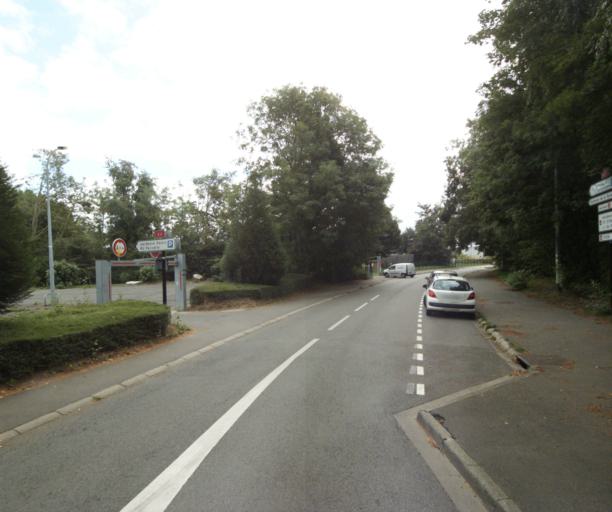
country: FR
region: Nord-Pas-de-Calais
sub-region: Departement du Nord
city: Villeneuve-d'Ascq
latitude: 50.6080
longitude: 3.1469
